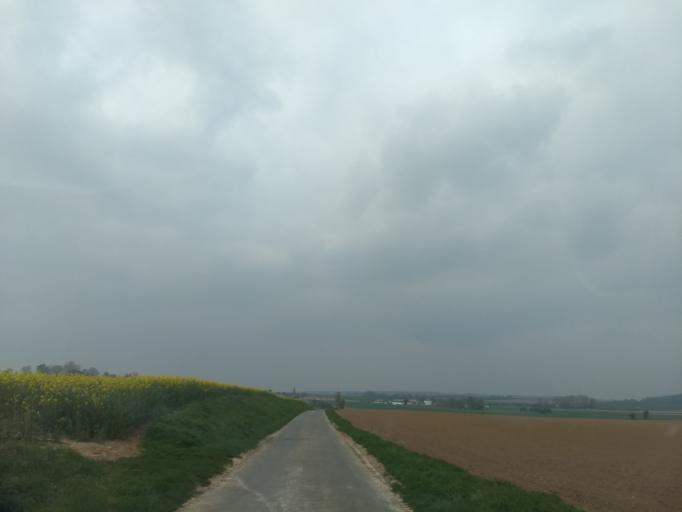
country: FR
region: Nord-Pas-de-Calais
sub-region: Departement du Pas-de-Calais
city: Mont-Saint-Eloi
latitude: 50.3438
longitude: 2.7019
